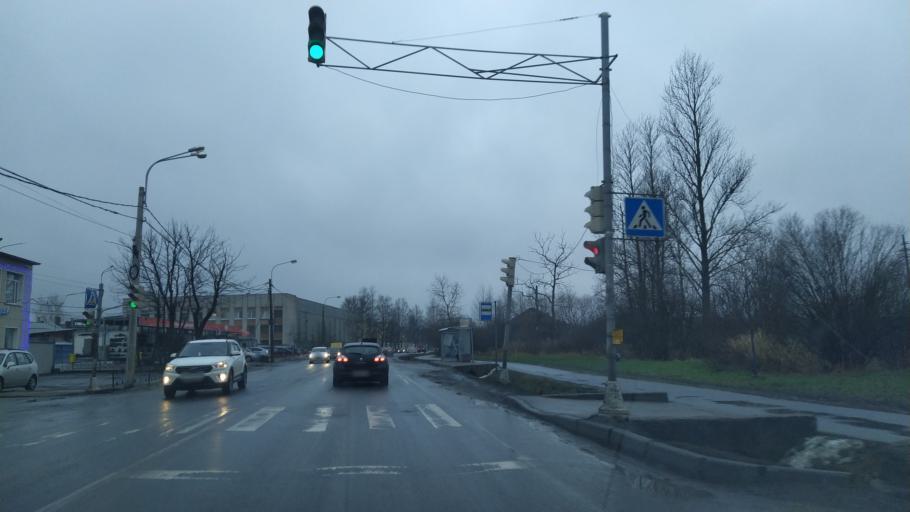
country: RU
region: St.-Petersburg
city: Tyarlevo
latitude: 59.7237
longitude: 30.4414
